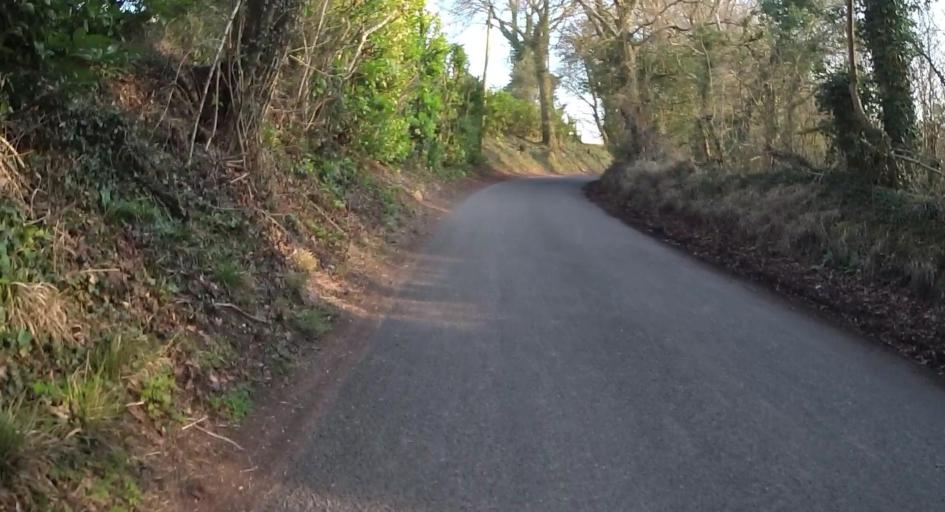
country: GB
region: England
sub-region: Hampshire
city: Alton
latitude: 51.1711
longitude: -1.0022
